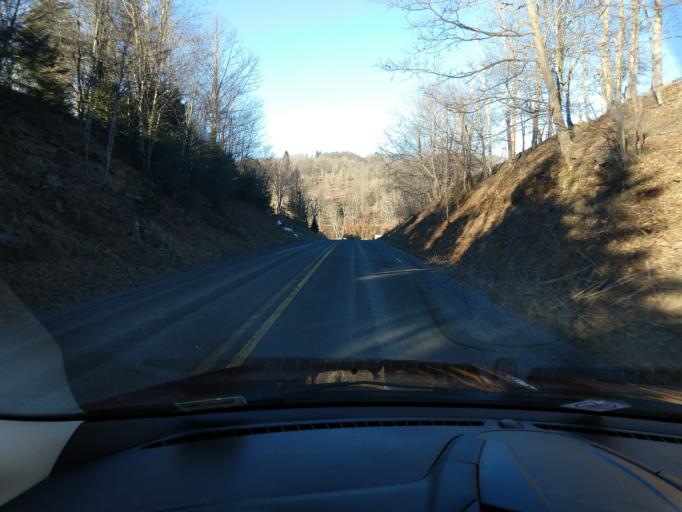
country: US
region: Virginia
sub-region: Highland County
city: Monterey
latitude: 38.4614
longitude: -79.6758
